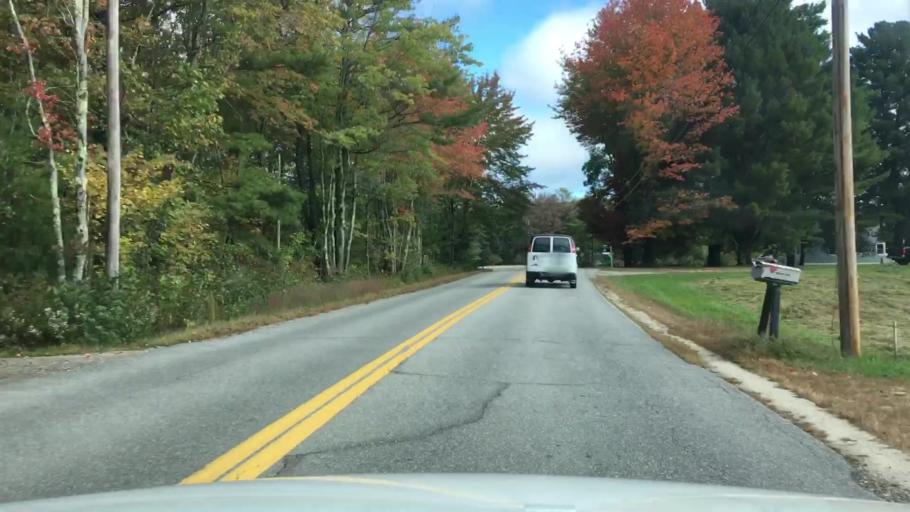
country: US
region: Maine
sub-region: Cumberland County
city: Brunswick
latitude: 43.9278
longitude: -69.9134
